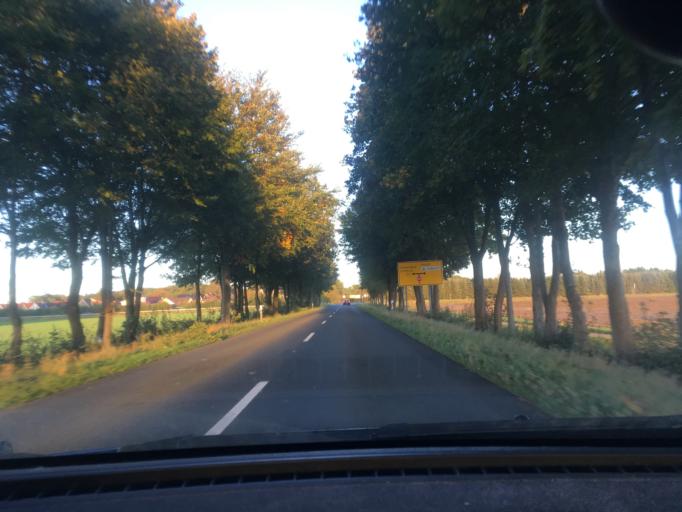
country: DE
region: Lower Saxony
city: Barendorf
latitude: 53.2256
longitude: 10.5119
